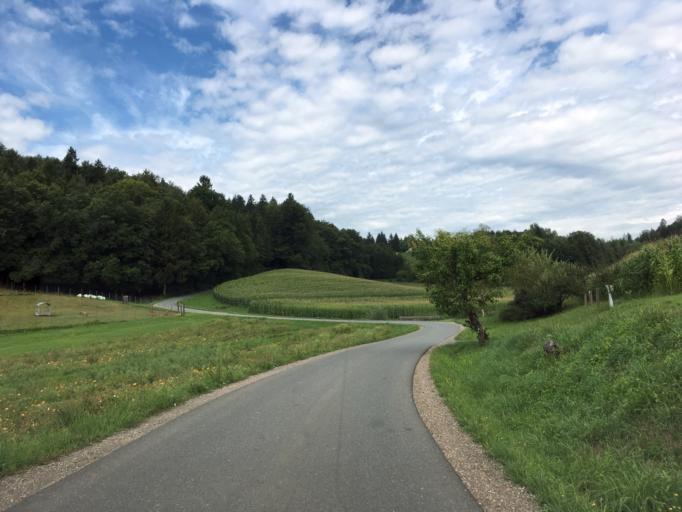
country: AT
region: Styria
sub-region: Politischer Bezirk Deutschlandsberg
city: Wettmannstatten
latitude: 46.7928
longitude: 15.3975
